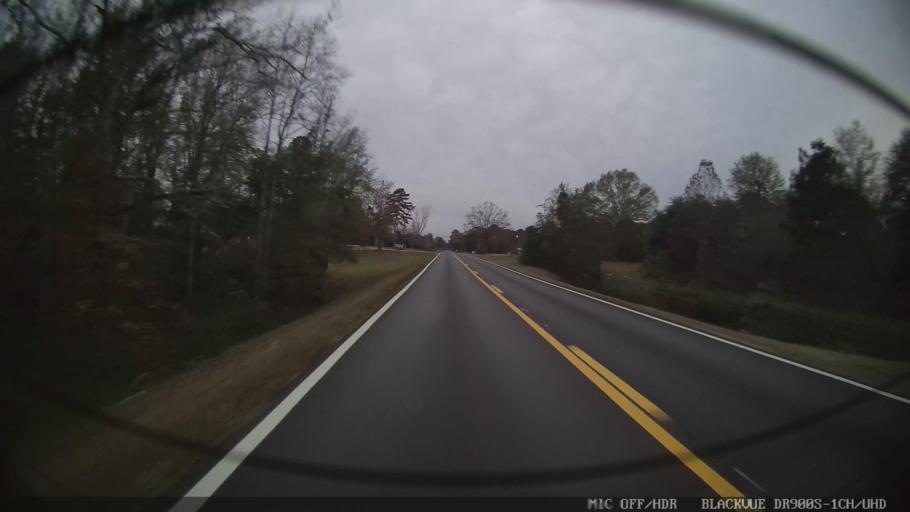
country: US
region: Mississippi
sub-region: Clarke County
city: Quitman
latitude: 32.0541
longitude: -88.6869
